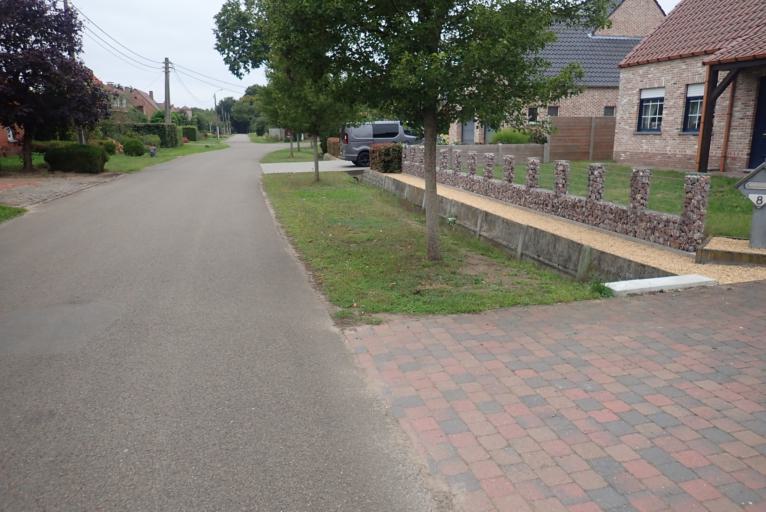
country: BE
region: Flanders
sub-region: Provincie Antwerpen
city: Lille
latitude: 51.2243
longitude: 4.8832
